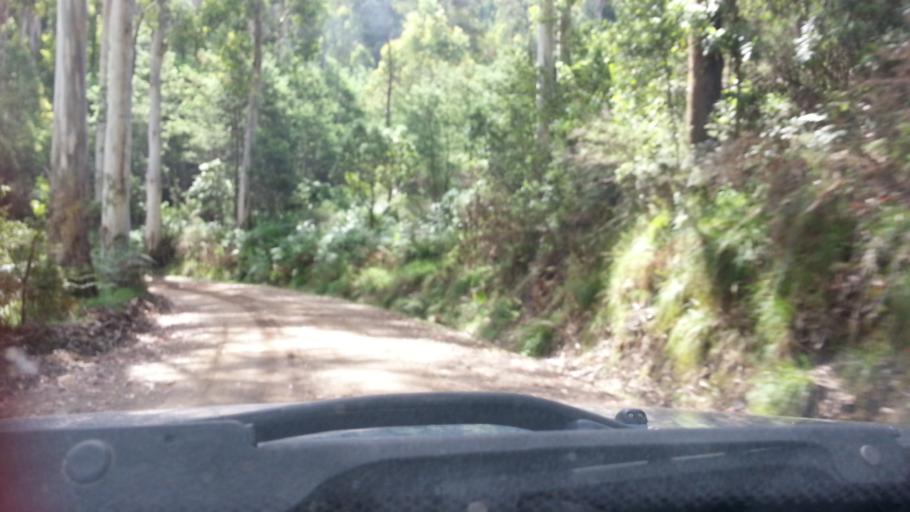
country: AU
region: Victoria
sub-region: Alpine
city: Mount Beauty
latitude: -36.6849
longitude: 147.2451
